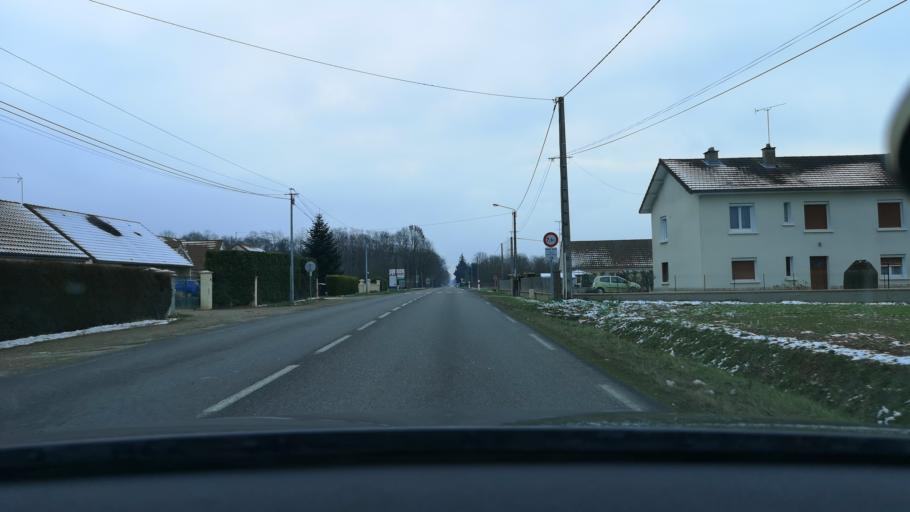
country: FR
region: Bourgogne
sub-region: Departement de Saone-et-Loire
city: Saint-Marcel
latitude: 46.7834
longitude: 4.9324
